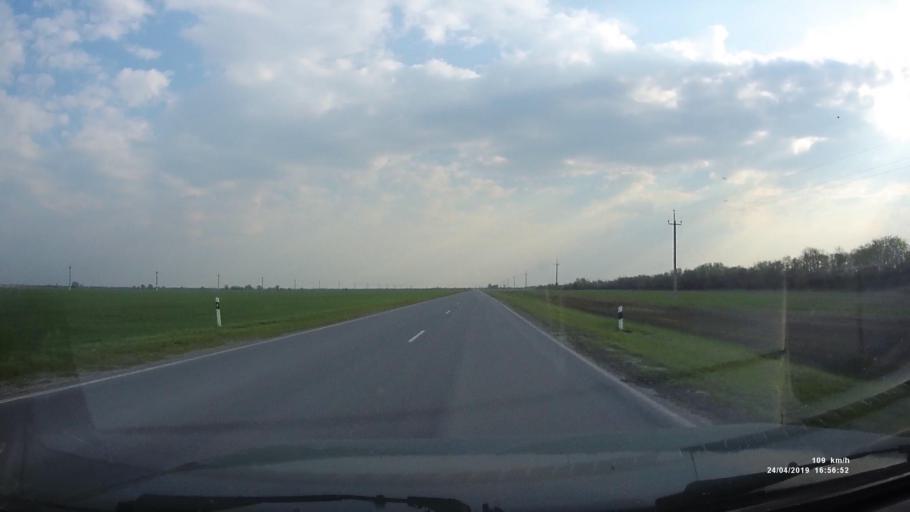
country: RU
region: Rostov
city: Proletarsk
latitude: 46.6453
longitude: 41.6738
